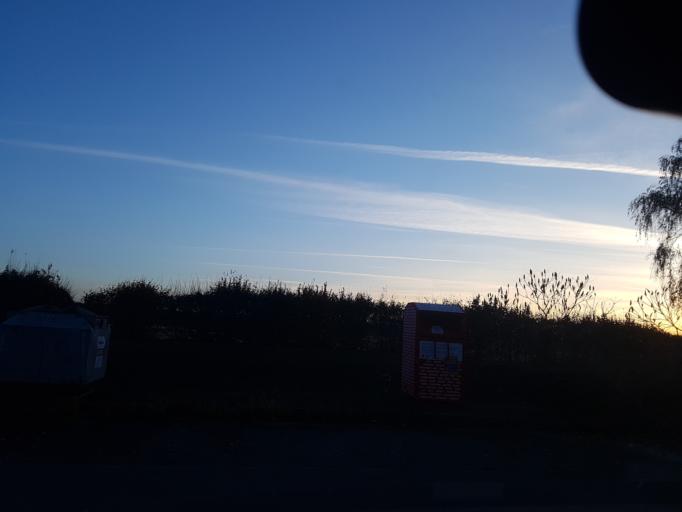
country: DE
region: Brandenburg
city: Finsterwalde
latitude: 51.6393
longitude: 13.6782
